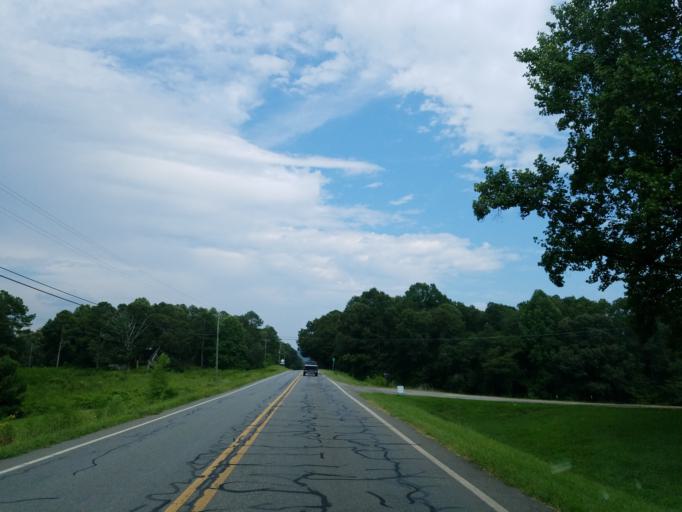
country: US
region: Georgia
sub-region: Gilmer County
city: Ellijay
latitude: 34.6423
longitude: -84.5444
